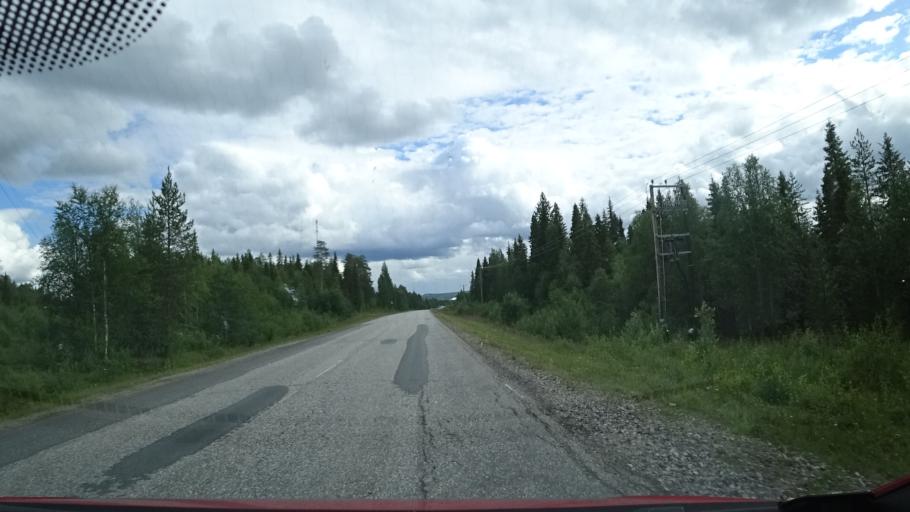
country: FI
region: Lapland
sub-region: Rovaniemi
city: Rovaniemi
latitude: 66.5488
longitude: 25.7005
